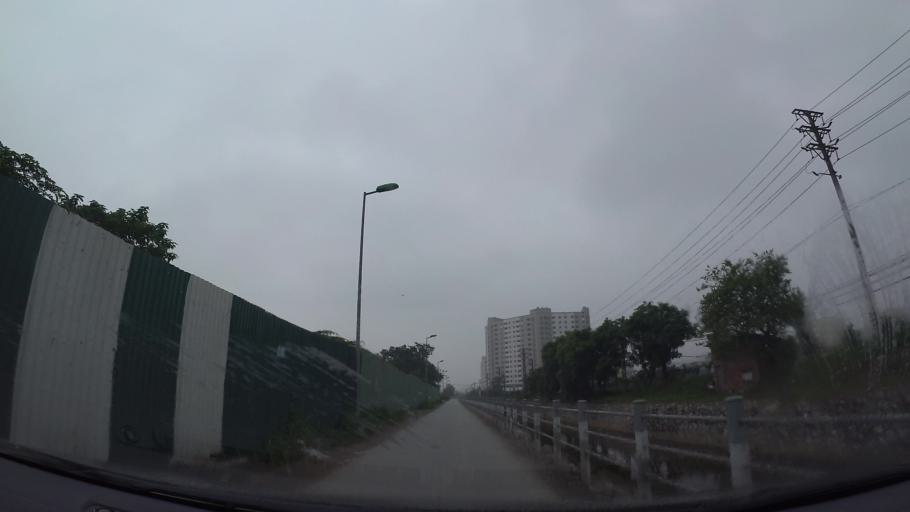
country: VN
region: Ha Noi
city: Van Dien
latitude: 20.9758
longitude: 105.8808
